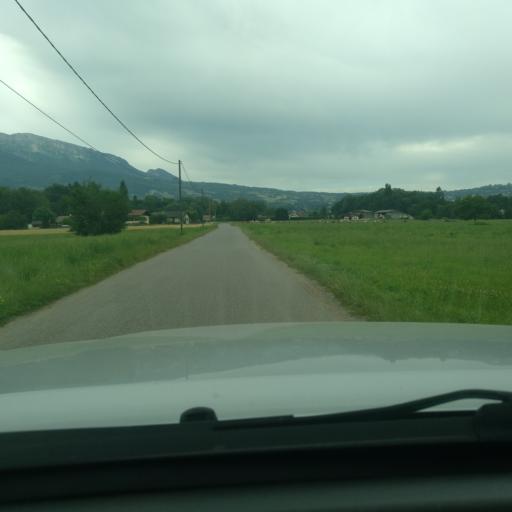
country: FR
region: Rhone-Alpes
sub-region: Departement de la Haute-Savoie
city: Amancy
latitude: 46.0875
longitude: 6.3500
